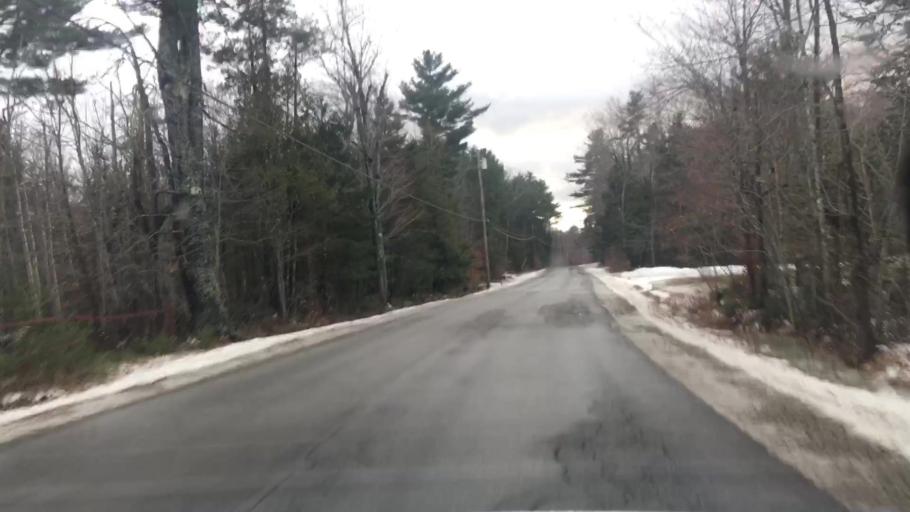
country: US
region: Maine
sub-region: Hancock County
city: Dedham
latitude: 44.6496
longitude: -68.7040
